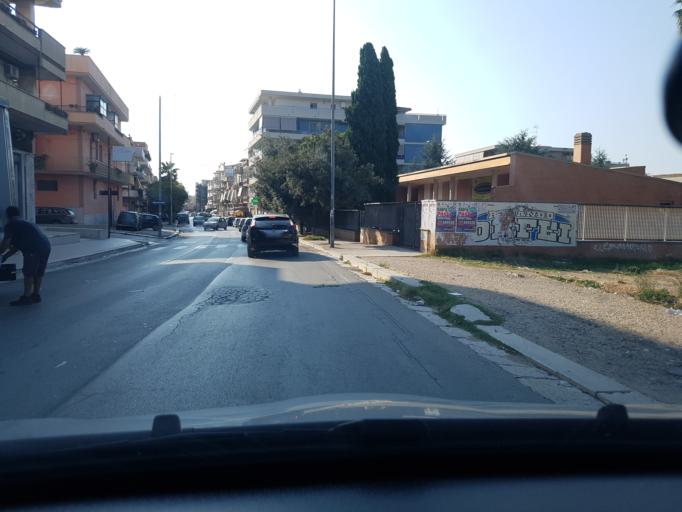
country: IT
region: Apulia
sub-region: Provincia di Foggia
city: Cerignola
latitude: 41.2703
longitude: 15.8983
